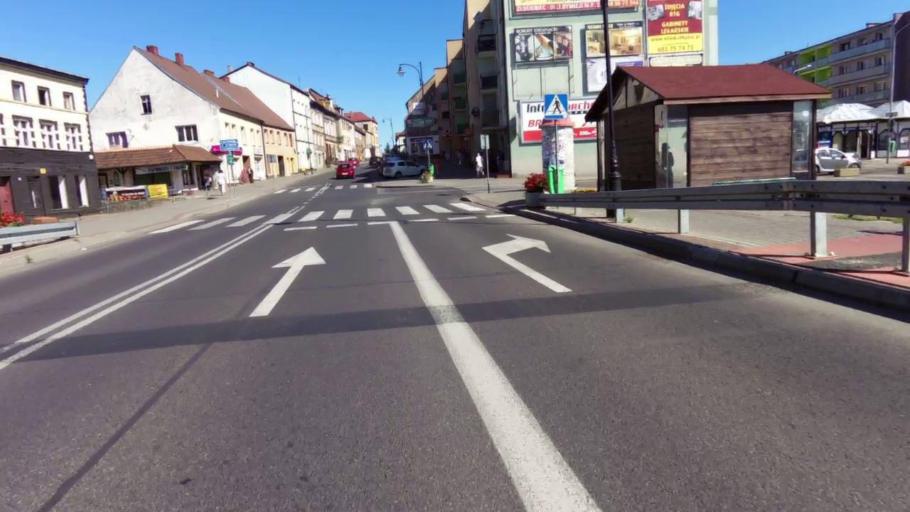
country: PL
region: West Pomeranian Voivodeship
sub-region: Powiat drawski
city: Zlocieniec
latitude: 53.5323
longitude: 16.0106
